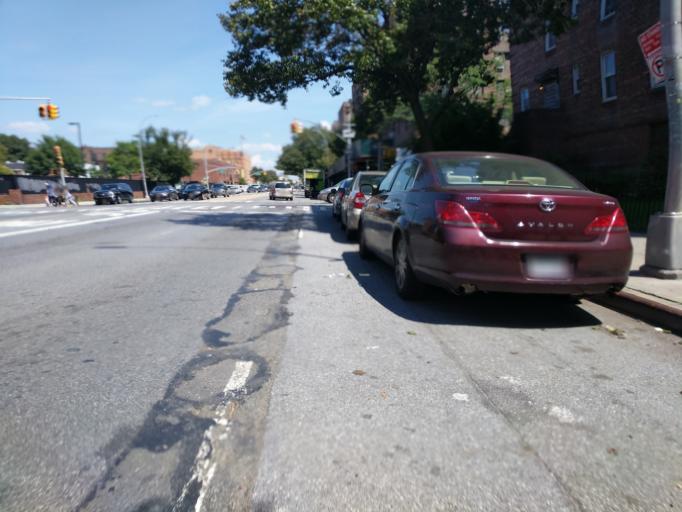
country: US
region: New York
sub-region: Queens County
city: Long Island City
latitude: 40.7563
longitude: -73.8775
